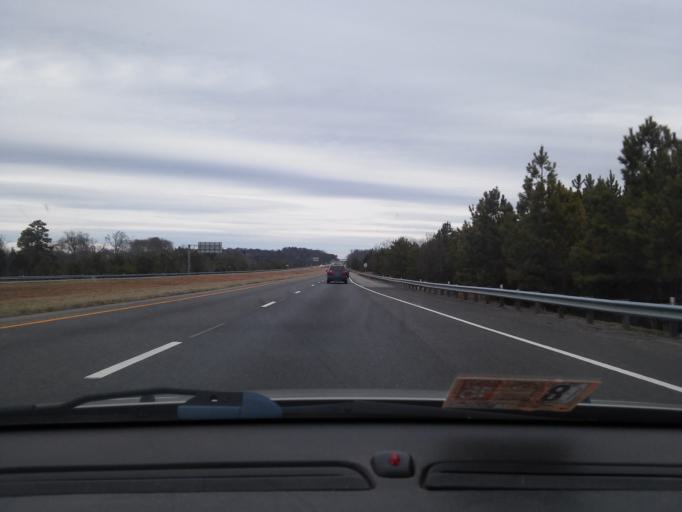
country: US
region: Virginia
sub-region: Henrico County
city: Short Pump
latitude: 37.5640
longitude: -77.6864
